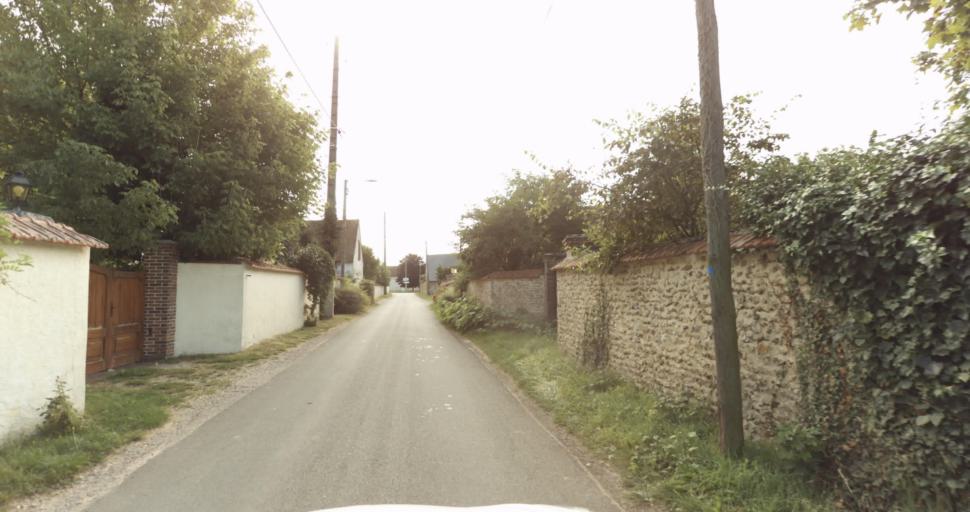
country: FR
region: Haute-Normandie
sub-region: Departement de l'Eure
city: Nonancourt
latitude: 48.8393
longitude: 1.1642
